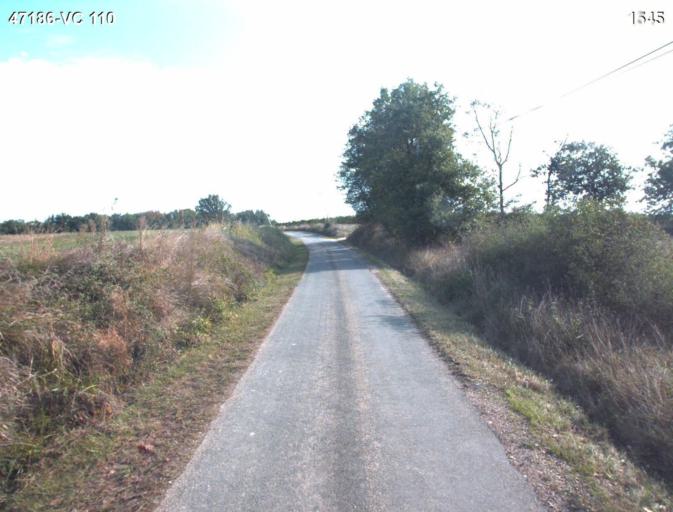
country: FR
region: Aquitaine
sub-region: Departement du Lot-et-Garonne
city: Port-Sainte-Marie
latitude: 44.1862
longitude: 0.4310
